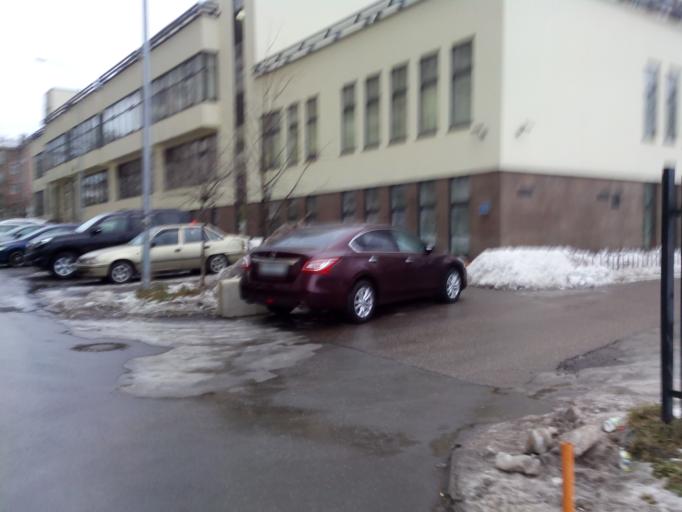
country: RU
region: Moscow
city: Ostankinskiy
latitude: 55.8226
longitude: 37.6249
